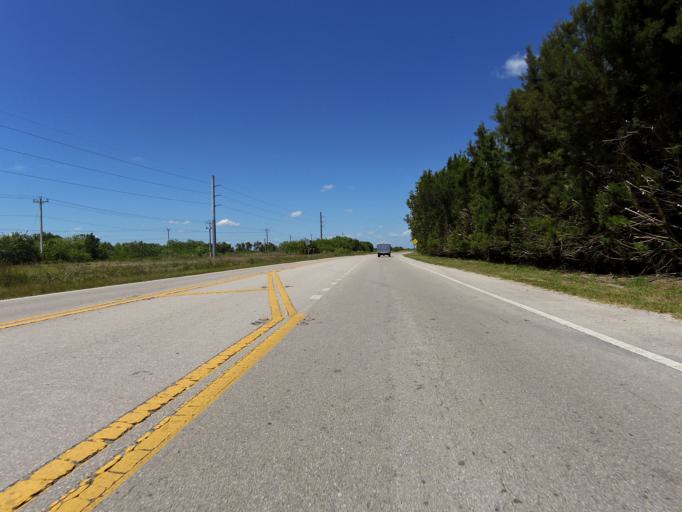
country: US
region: Florida
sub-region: Collier County
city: Immokalee
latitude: 26.3508
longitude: -81.4168
